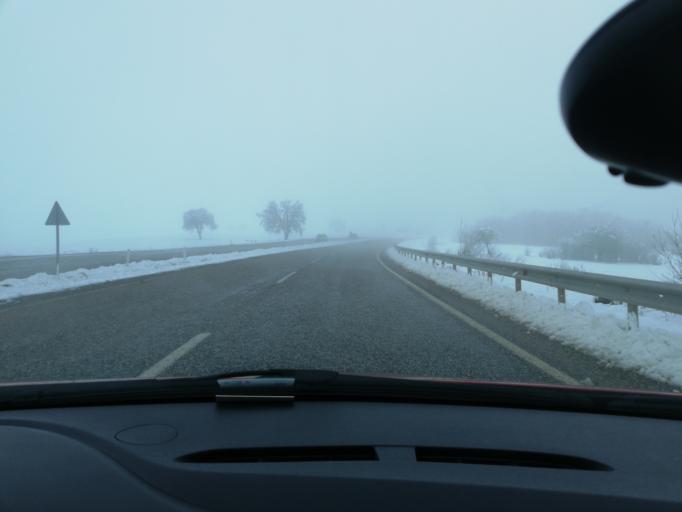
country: TR
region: Kastamonu
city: Akkaya
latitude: 41.2961
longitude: 33.4986
